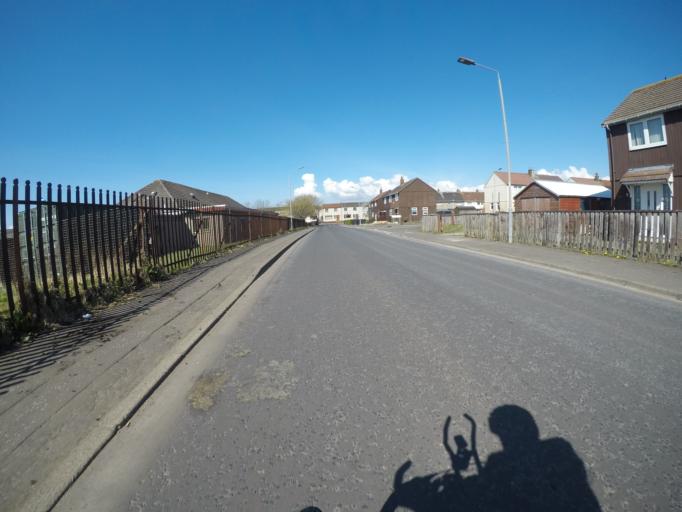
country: GB
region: Scotland
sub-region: North Ayrshire
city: Irvine
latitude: 55.6210
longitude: -4.6622
